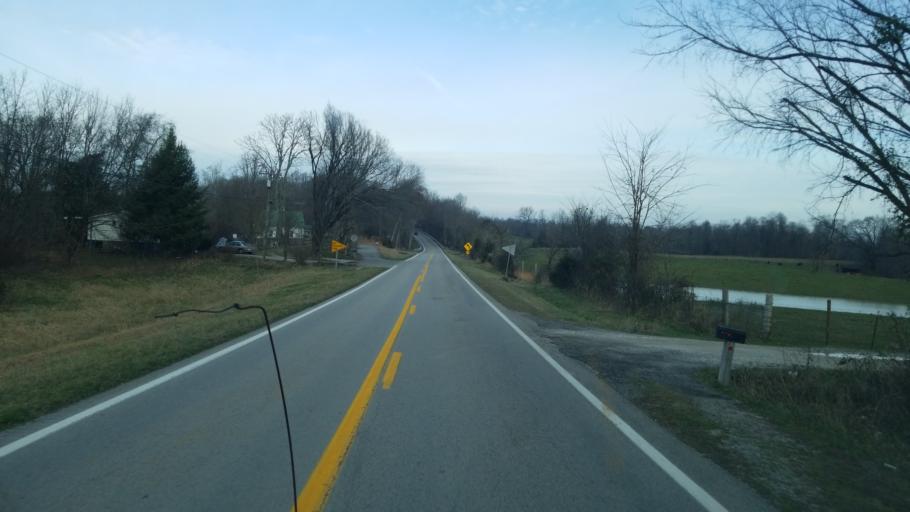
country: US
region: Kentucky
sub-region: Clinton County
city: Albany
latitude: 36.8151
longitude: -85.1817
